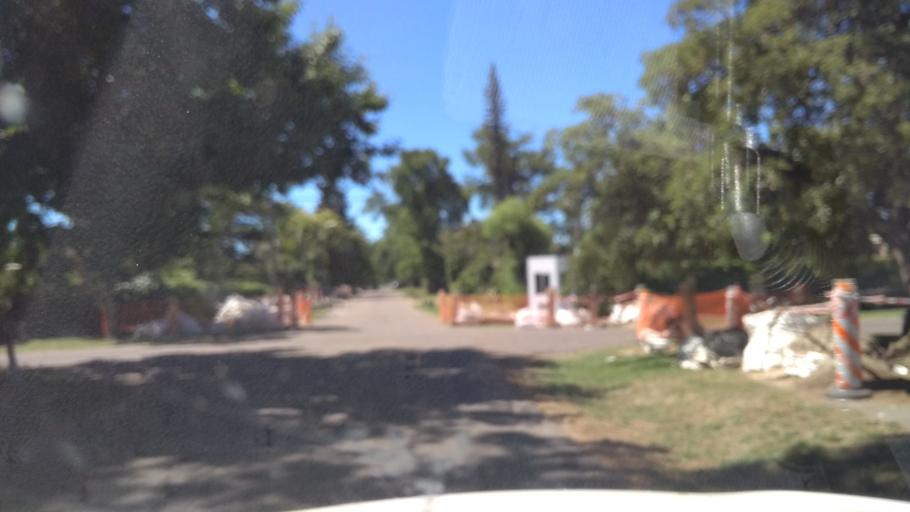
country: UY
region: Canelones
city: Paso de Carrasco
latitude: -34.8730
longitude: -56.0611
